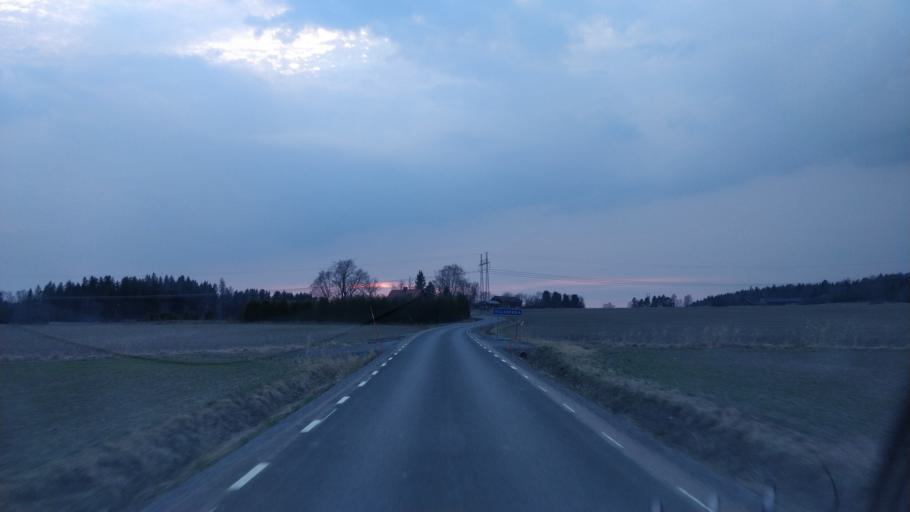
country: SE
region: Uppsala
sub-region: Enkopings Kommun
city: Orsundsbro
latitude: 59.7207
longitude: 17.2356
